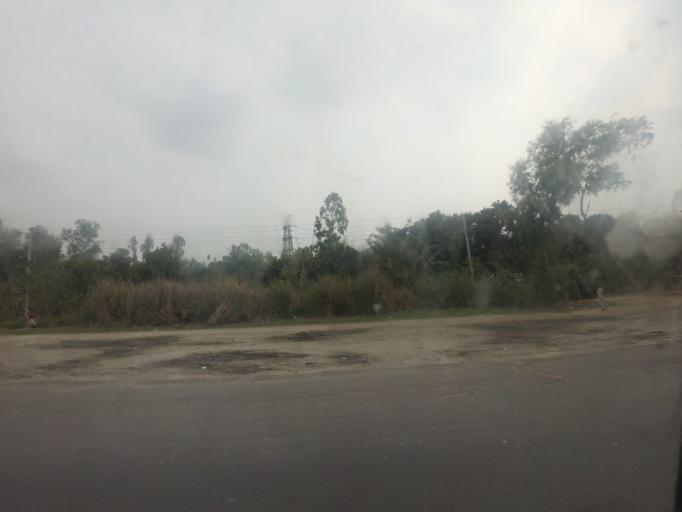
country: BD
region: Rajshahi
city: Sirajganj
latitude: 24.3924
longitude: 89.7122
